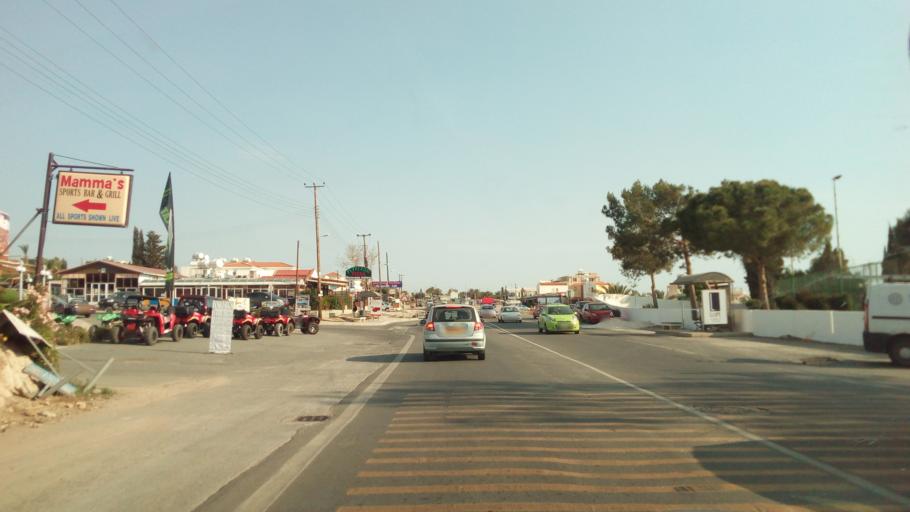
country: CY
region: Pafos
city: Chlorakas
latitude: 34.8057
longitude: 32.3970
